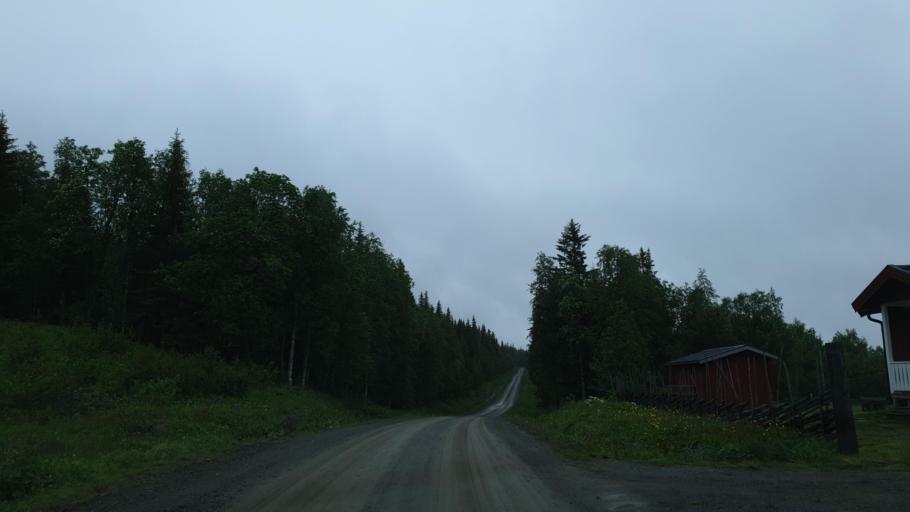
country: SE
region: Vaesterbotten
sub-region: Vilhelmina Kommun
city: Sjoberg
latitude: 65.3432
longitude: 15.8794
